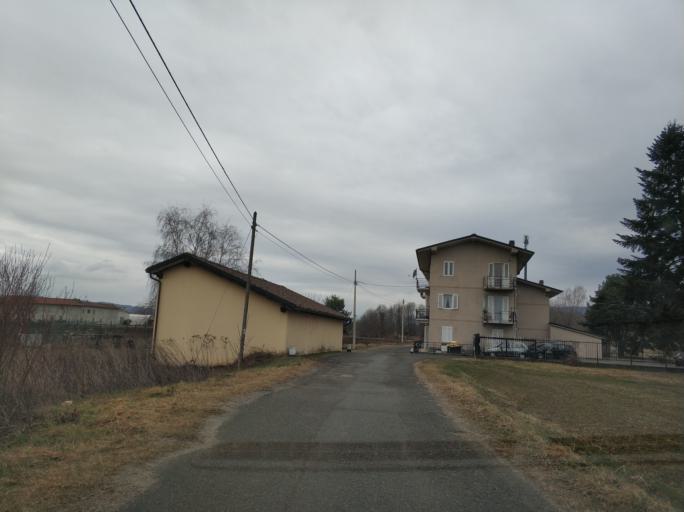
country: IT
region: Piedmont
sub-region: Provincia di Torino
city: Pavone Canavese
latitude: 45.4369
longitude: 7.8750
